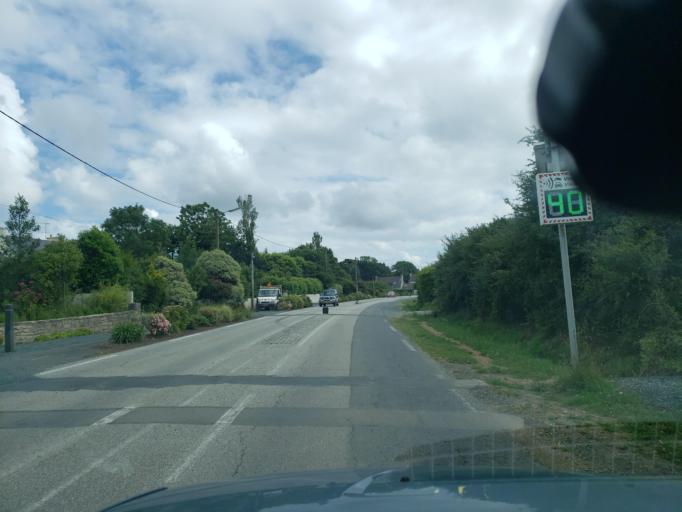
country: FR
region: Brittany
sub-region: Departement du Finistere
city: Plomeur
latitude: 47.8463
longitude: -4.2826
